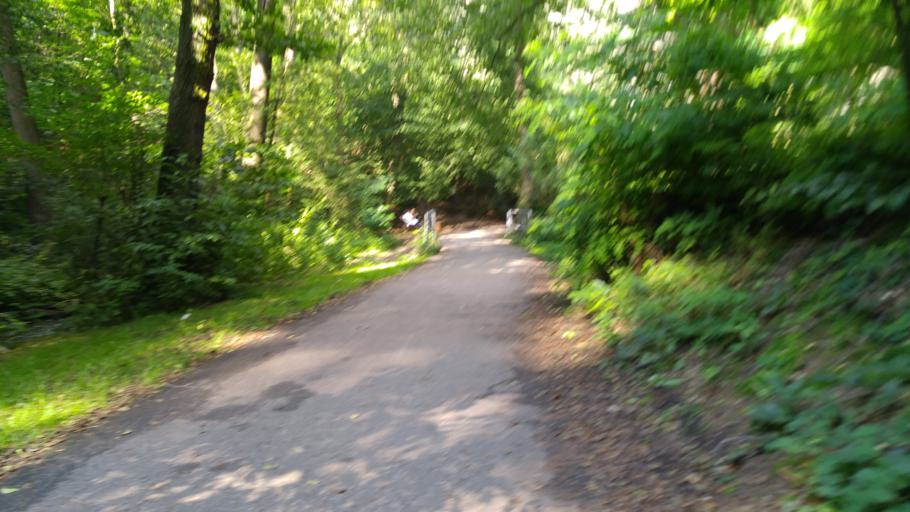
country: CZ
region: Central Bohemia
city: Horomerice
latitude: 50.1023
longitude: 14.3210
